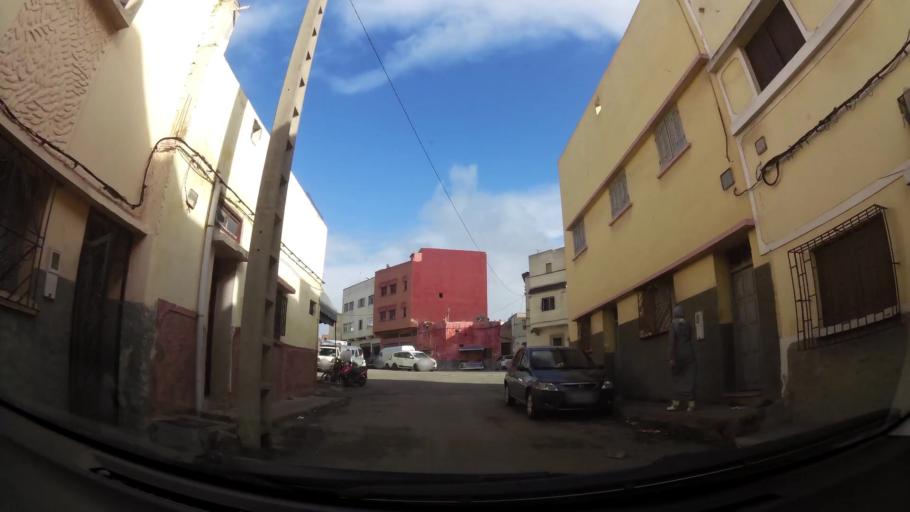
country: MA
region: Doukkala-Abda
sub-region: El-Jadida
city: El Jadida
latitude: 33.2563
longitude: -8.5161
